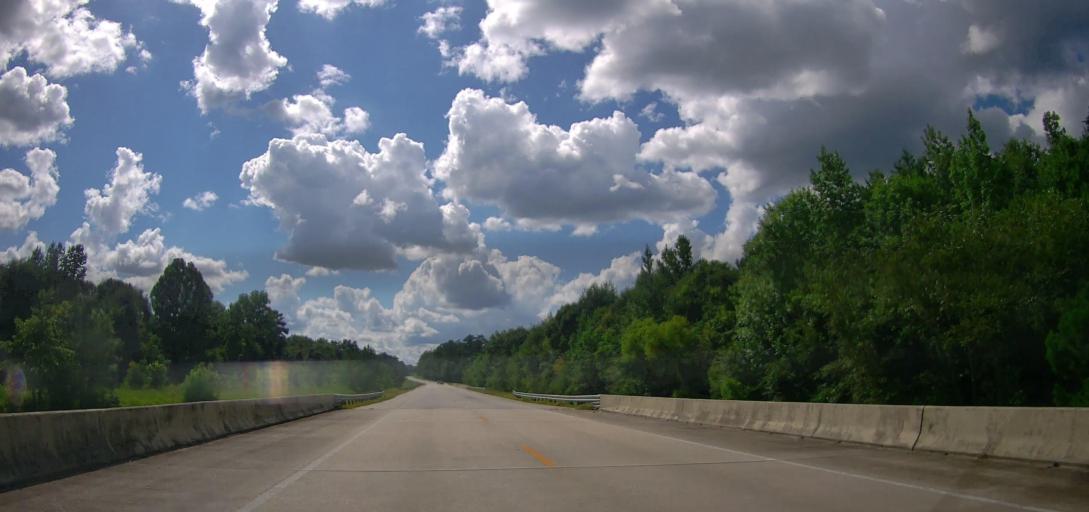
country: US
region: Alabama
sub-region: Lee County
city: Auburn
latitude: 32.4500
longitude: -85.5241
